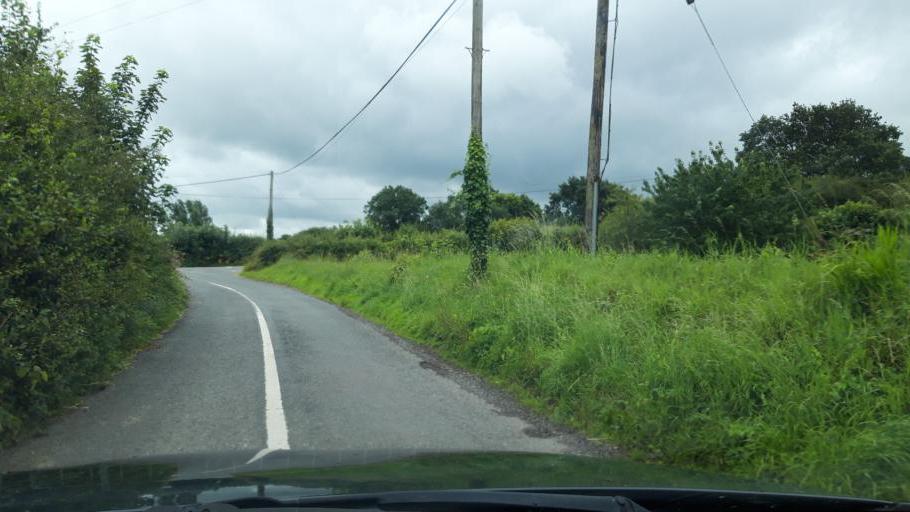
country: IE
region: Munster
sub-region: County Cork
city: Castlemartyr
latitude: 52.1294
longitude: -8.0039
